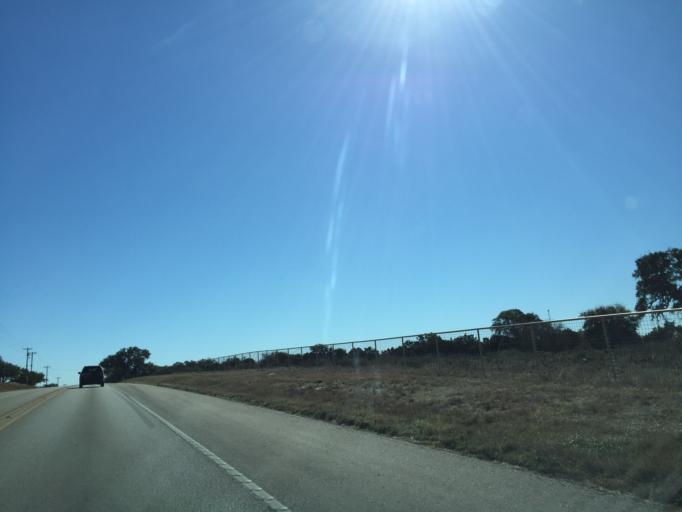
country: US
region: Texas
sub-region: Comal County
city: Canyon Lake
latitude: 29.7759
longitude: -98.3066
